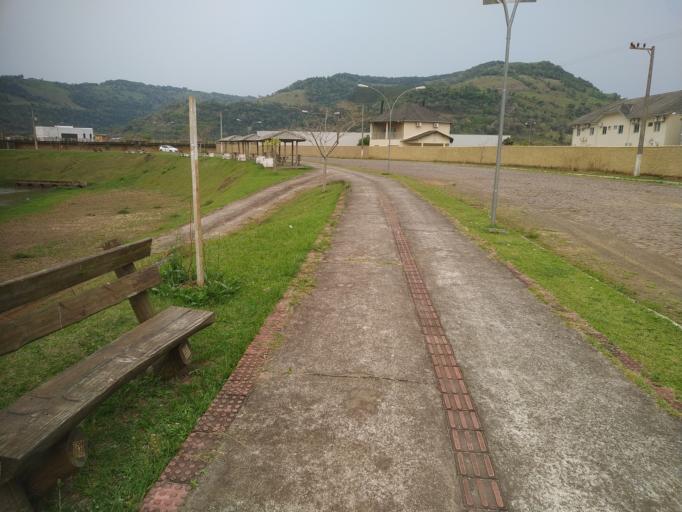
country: BR
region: Santa Catarina
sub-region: Chapeco
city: Chapeco
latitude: -27.2820
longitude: -52.6943
